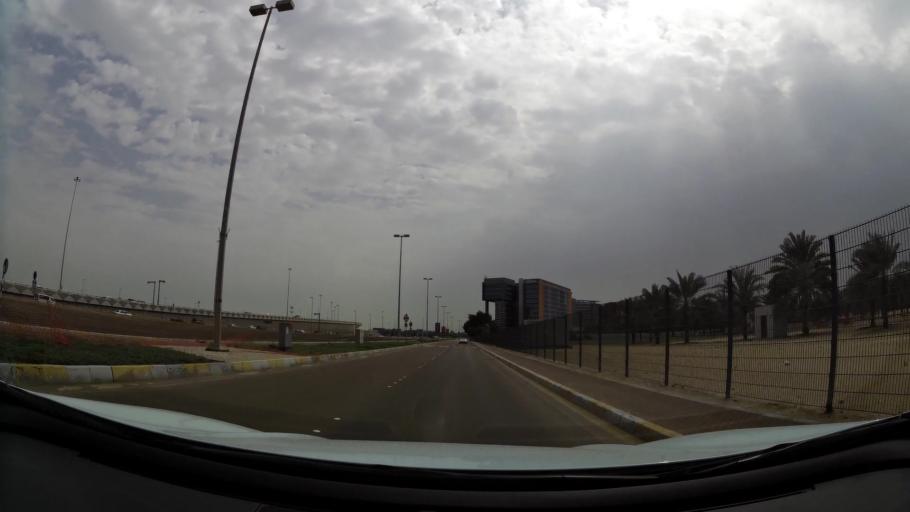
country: AE
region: Abu Dhabi
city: Abu Dhabi
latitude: 24.4281
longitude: 54.4700
